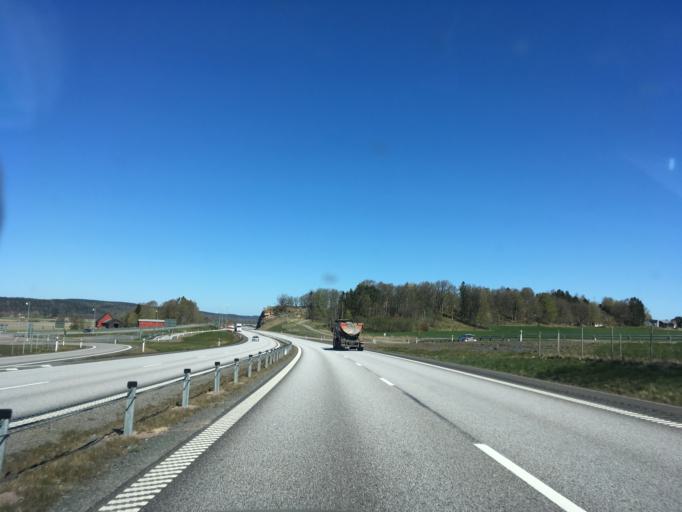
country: SE
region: Vaestra Goetaland
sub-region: Ale Kommun
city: Skepplanda
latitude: 57.9924
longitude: 12.1627
